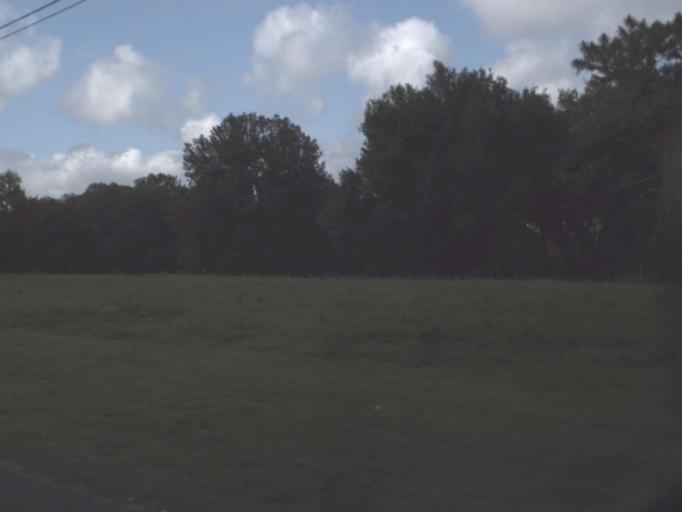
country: US
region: Florida
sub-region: Lake County
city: Lady Lake
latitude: 28.8959
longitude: -81.9096
